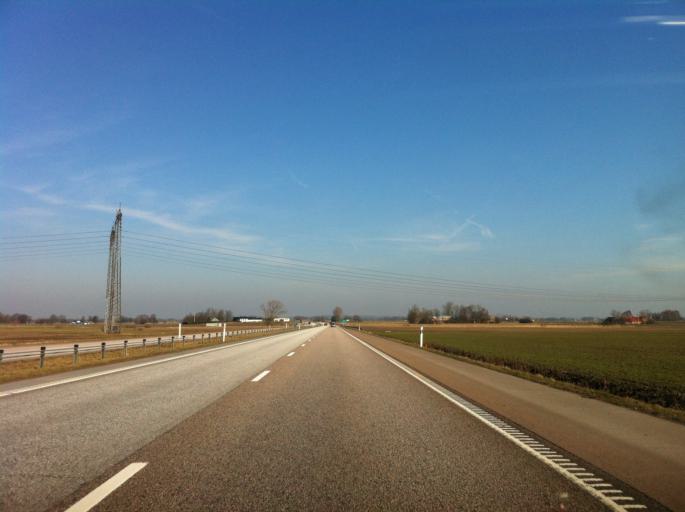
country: SE
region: Skane
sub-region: Angelholms Kommun
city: Strovelstorp
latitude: 56.1227
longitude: 12.8215
